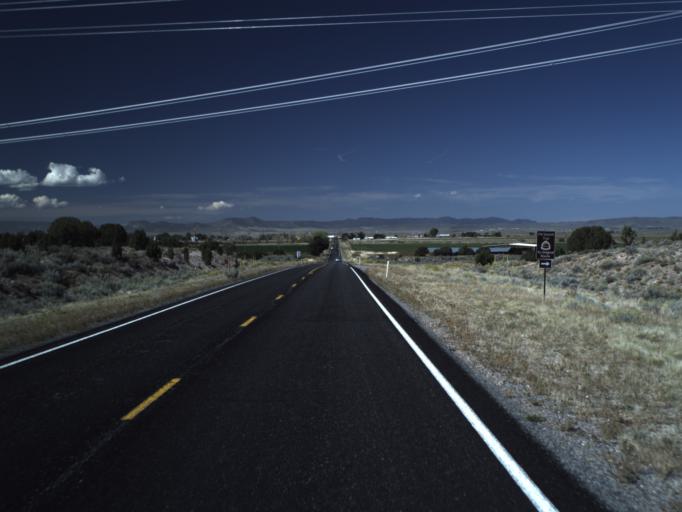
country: US
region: Utah
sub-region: Washington County
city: Enterprise
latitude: 37.6743
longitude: -113.5281
